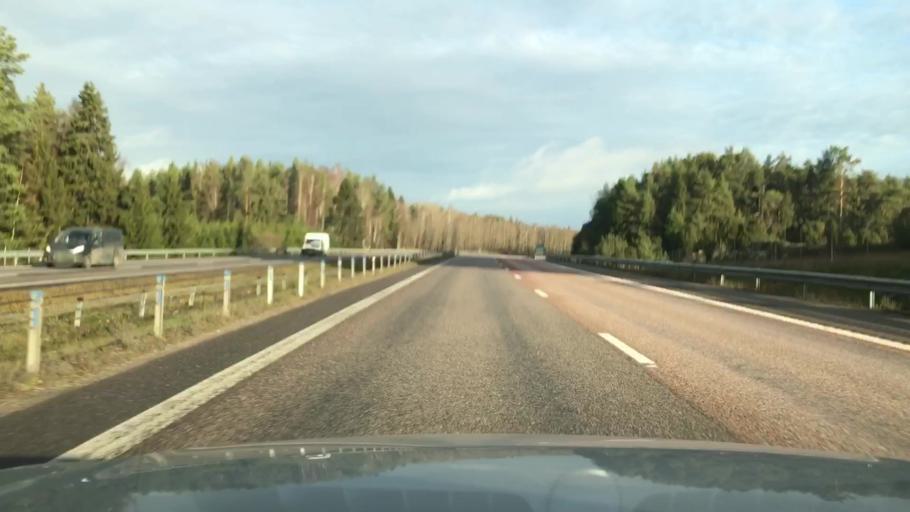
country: SE
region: Soedermanland
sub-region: Gnesta Kommun
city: Gnesta
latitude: 58.8708
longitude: 17.2267
